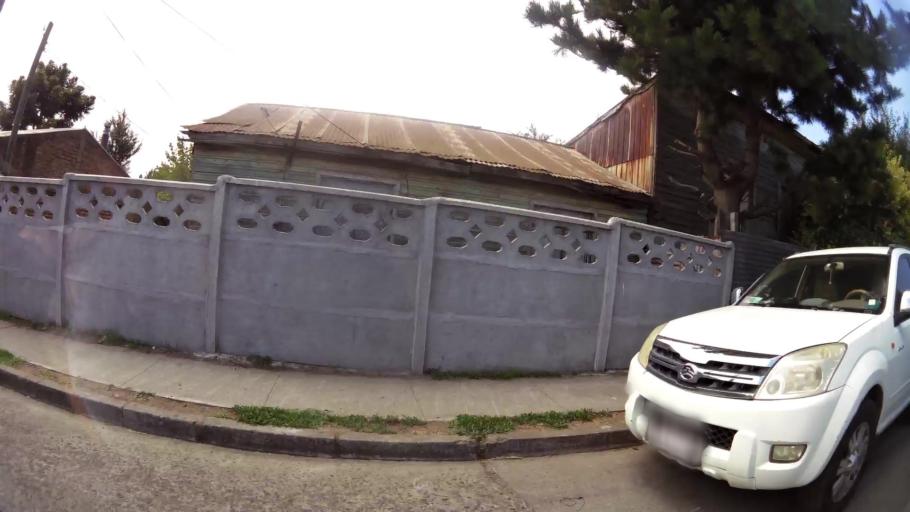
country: CL
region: Biobio
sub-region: Provincia de Concepcion
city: Concepcion
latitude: -36.8023
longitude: -73.0429
